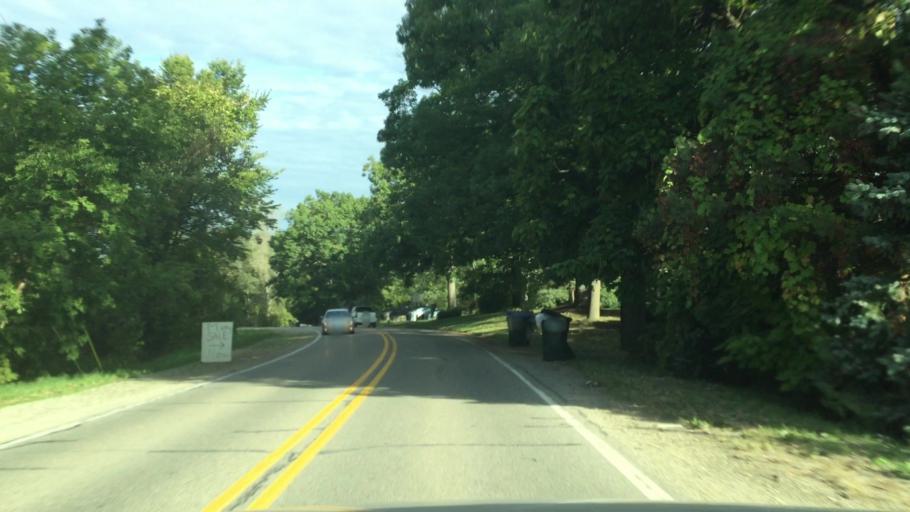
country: US
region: Michigan
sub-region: Livingston County
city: Howell
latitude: 42.5919
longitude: -83.9015
